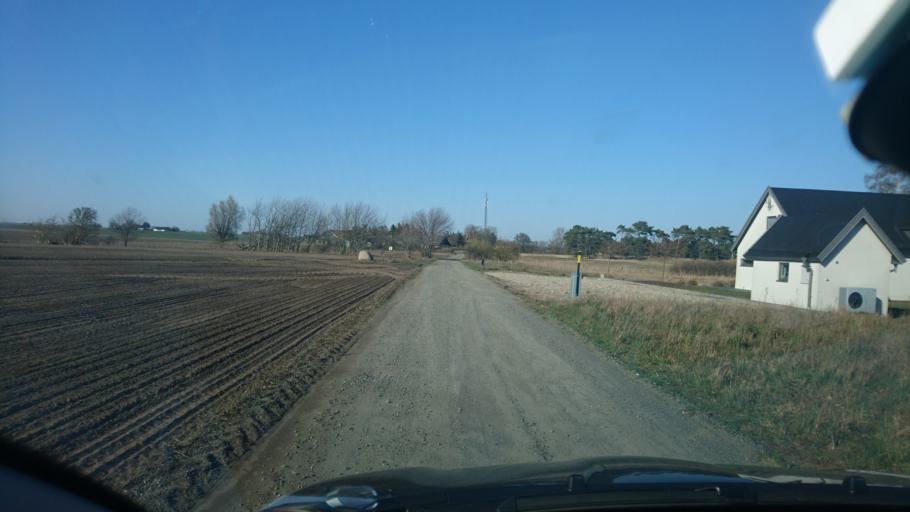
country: SE
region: Skane
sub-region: Simrishamns Kommun
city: Simrishamn
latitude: 55.4178
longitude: 14.2058
